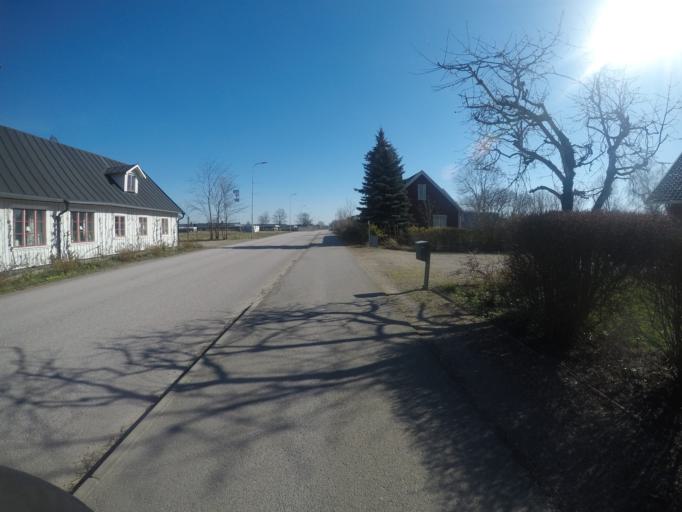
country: SE
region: Halland
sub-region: Laholms Kommun
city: Laholm
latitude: 56.5089
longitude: 13.0527
